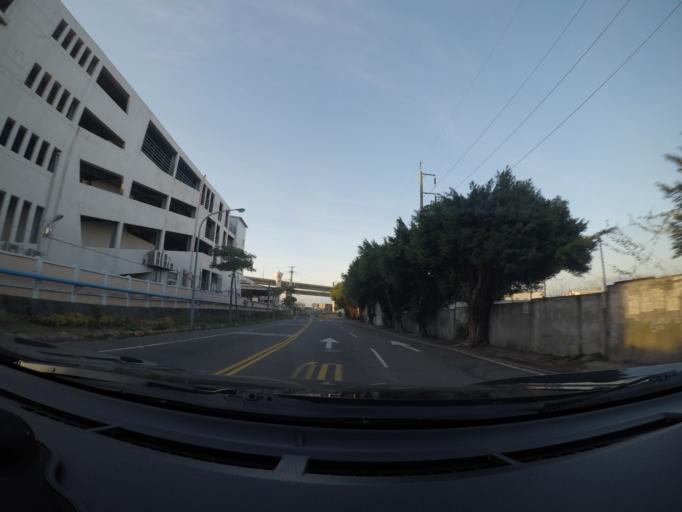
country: TW
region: Taiwan
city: Taoyuan City
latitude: 24.9934
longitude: 121.2455
